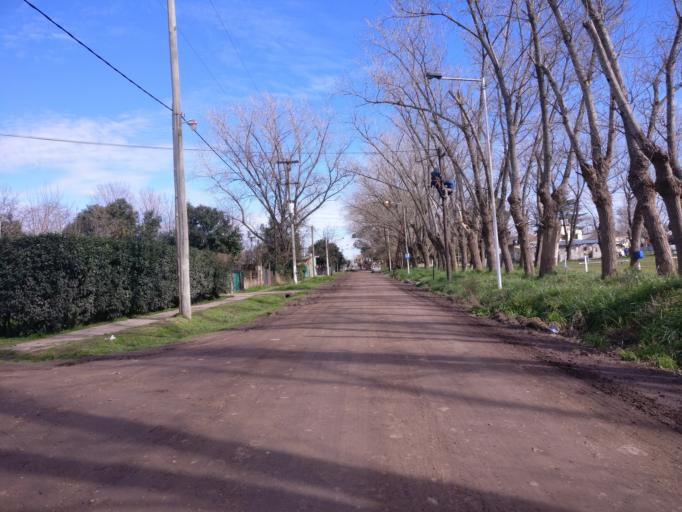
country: AR
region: Buenos Aires
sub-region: Partido de Ezeiza
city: Ezeiza
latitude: -34.9385
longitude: -58.6113
